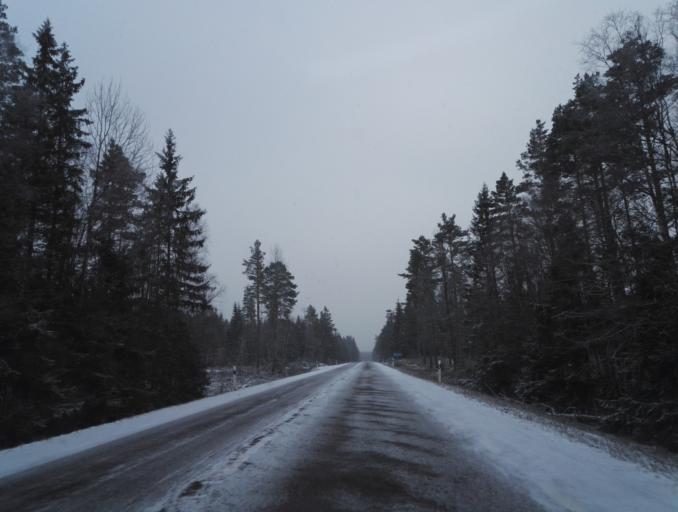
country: SE
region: Kronoberg
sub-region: Uppvidinge Kommun
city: Lenhovda
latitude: 56.8903
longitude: 15.3727
